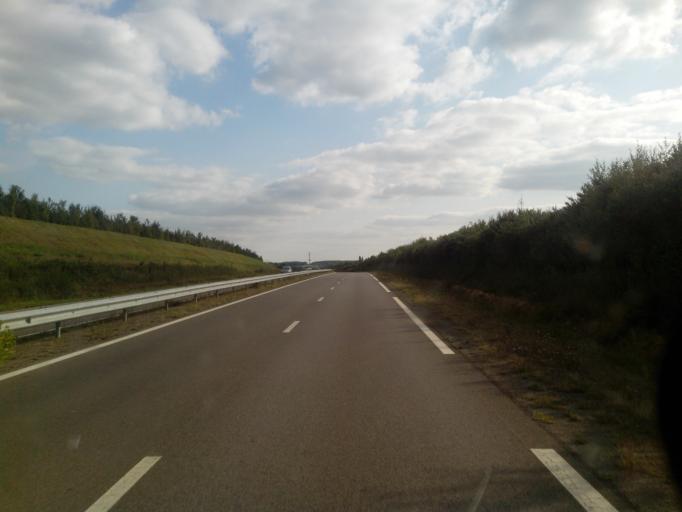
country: FR
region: Brittany
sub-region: Departement d'Ille-et-Vilaine
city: Betton
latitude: 48.1689
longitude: -1.6264
